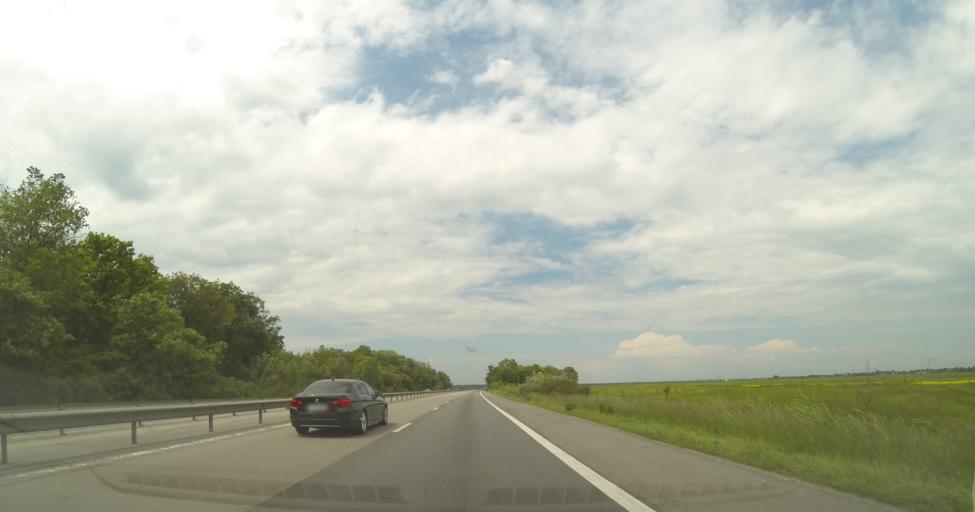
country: RO
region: Dambovita
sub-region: Comuna Corbii Mari
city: Grozavesti
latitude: 44.5830
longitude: 25.4676
